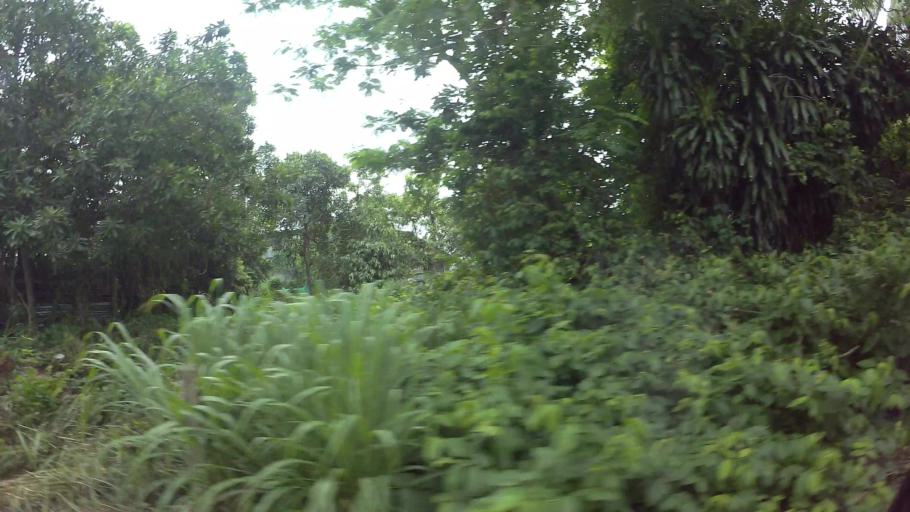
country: TH
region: Chon Buri
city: Si Racha
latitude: 13.1799
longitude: 100.9776
